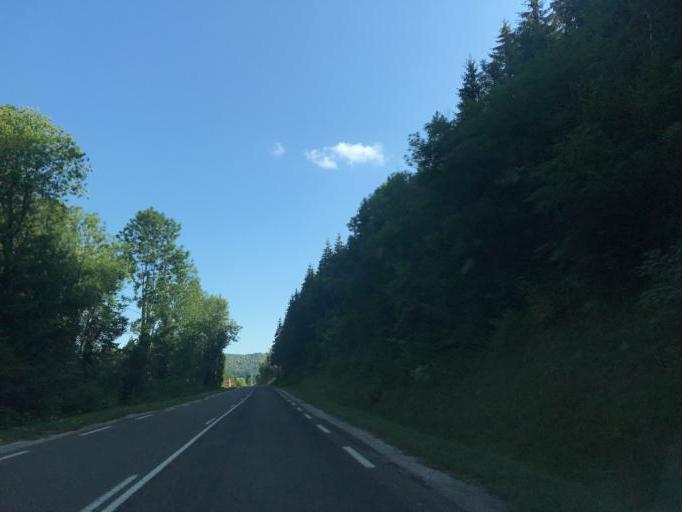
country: FR
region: Franche-Comte
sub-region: Departement du Jura
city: Moirans-en-Montagne
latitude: 46.4037
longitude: 5.7340
